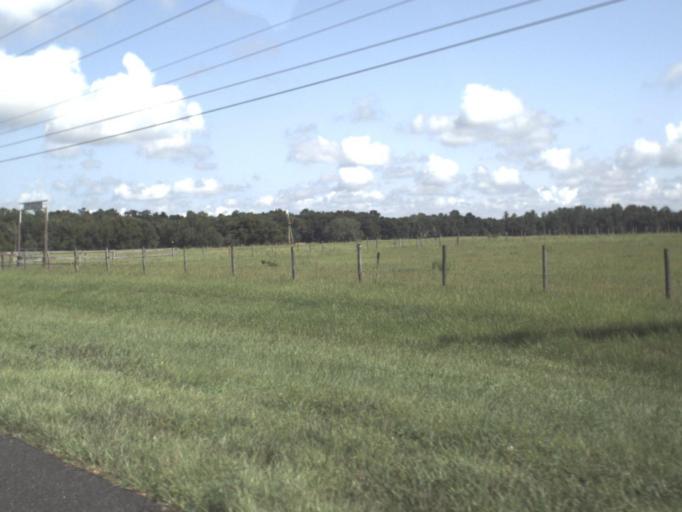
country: US
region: Florida
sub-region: Hernando County
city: Hill 'n Dale
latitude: 28.5258
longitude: -82.3141
